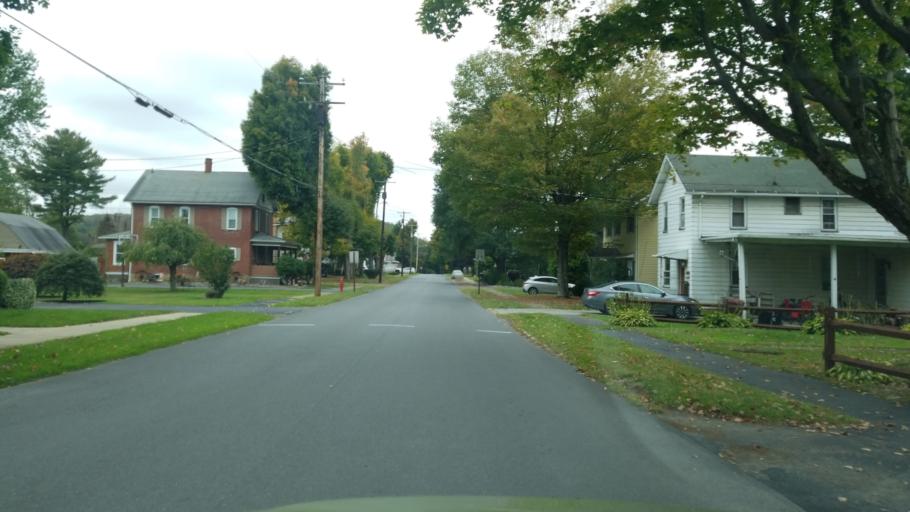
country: US
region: Pennsylvania
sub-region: Clearfield County
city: Curwensville
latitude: 40.9717
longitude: -78.5149
